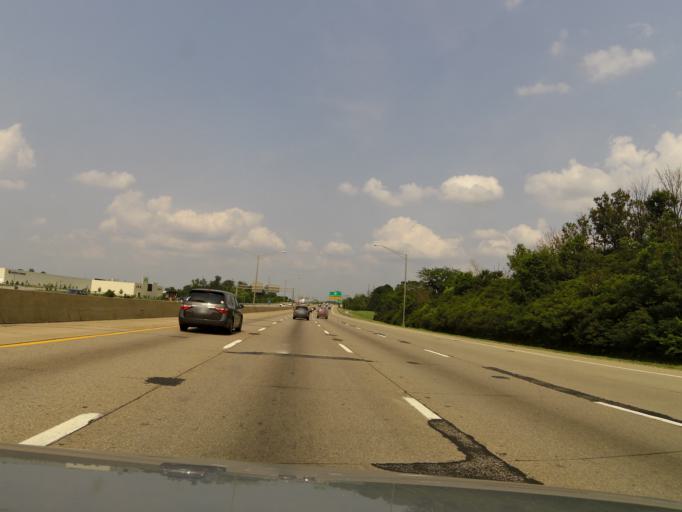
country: US
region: Kentucky
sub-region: Kenton County
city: Crestview Hills
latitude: 39.0393
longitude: -84.5890
